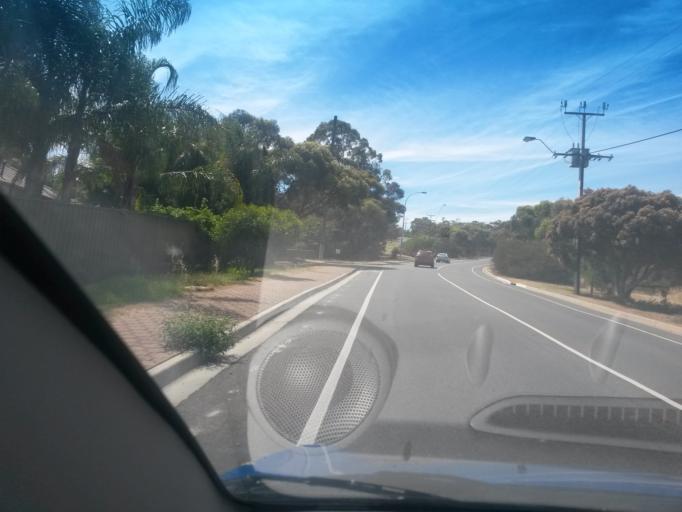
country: AU
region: South Australia
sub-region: Salisbury
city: Salisbury
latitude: -34.7698
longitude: 138.6837
